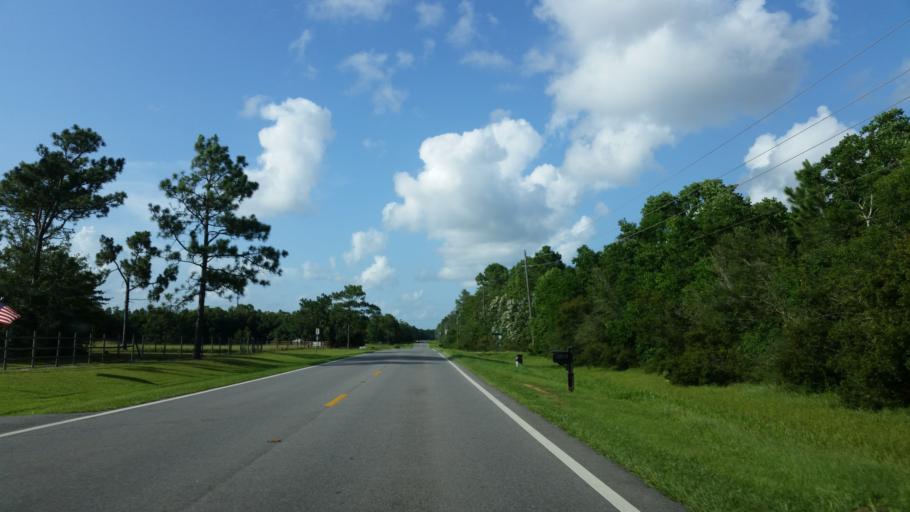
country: US
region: Florida
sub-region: Santa Rosa County
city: Bagdad
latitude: 30.5496
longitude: -87.0447
